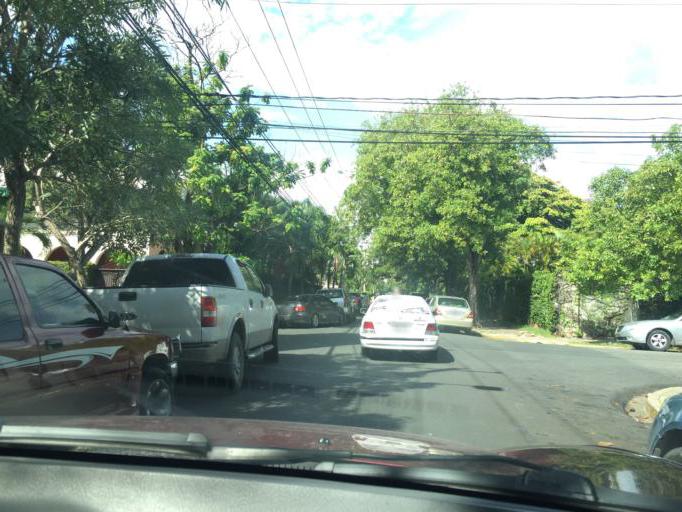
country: DO
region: Nacional
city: Ciudad Nueva
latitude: 18.4652
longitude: -69.9003
